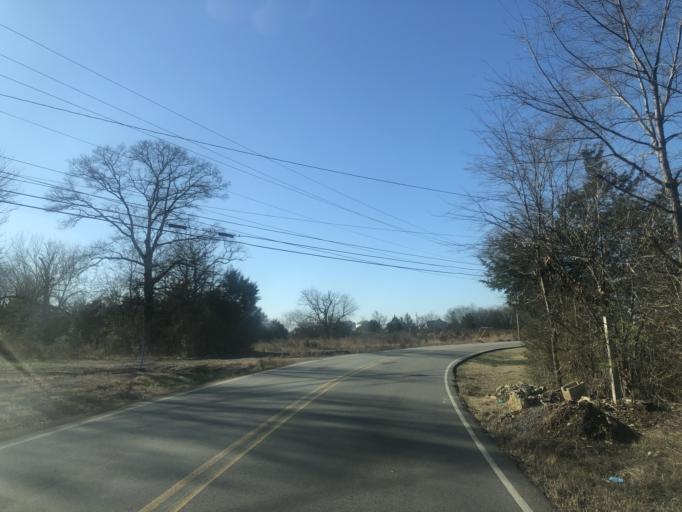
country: US
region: Tennessee
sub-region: Rutherford County
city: Smyrna
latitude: 35.9612
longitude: -86.5368
